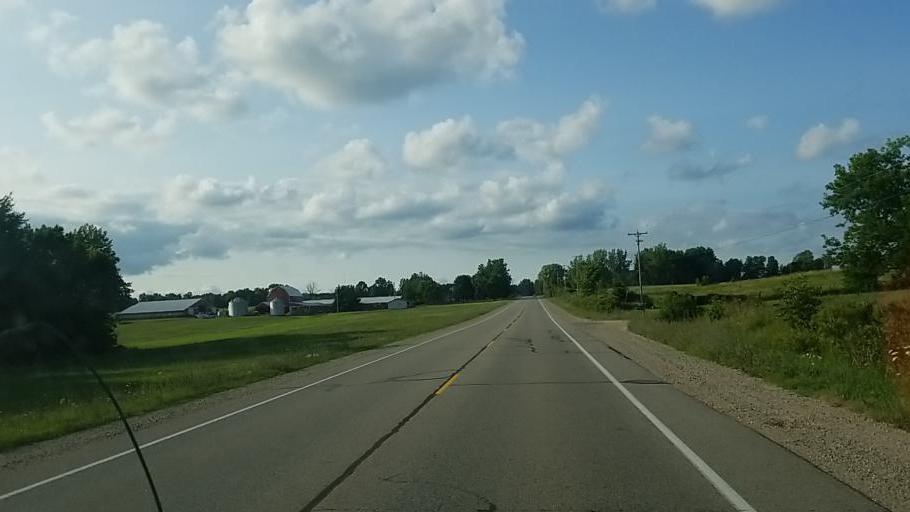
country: US
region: Michigan
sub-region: Kent County
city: Lowell
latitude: 43.0240
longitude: -85.3519
